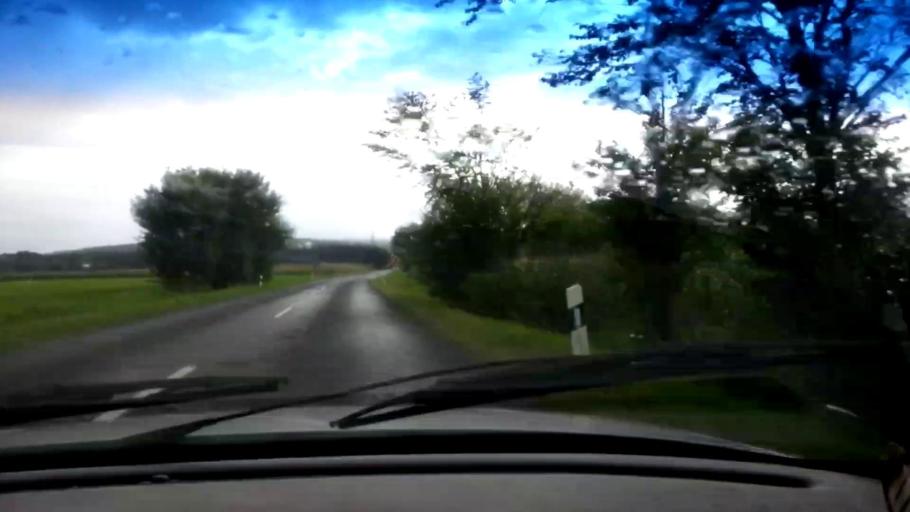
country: DE
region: Bavaria
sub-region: Upper Palatinate
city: Mitterteich
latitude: 50.0001
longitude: 12.2418
